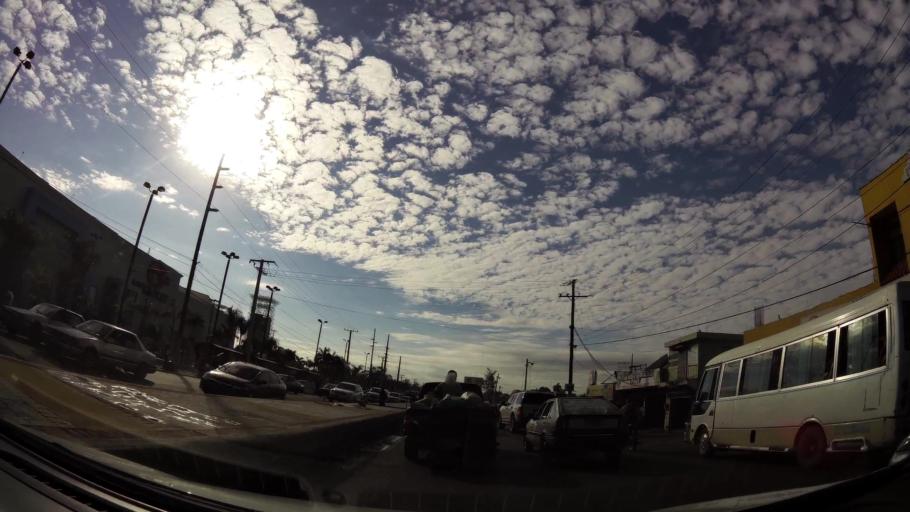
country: DO
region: Santo Domingo
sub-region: Santo Domingo
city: Santo Domingo Este
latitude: 18.5057
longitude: -69.8574
